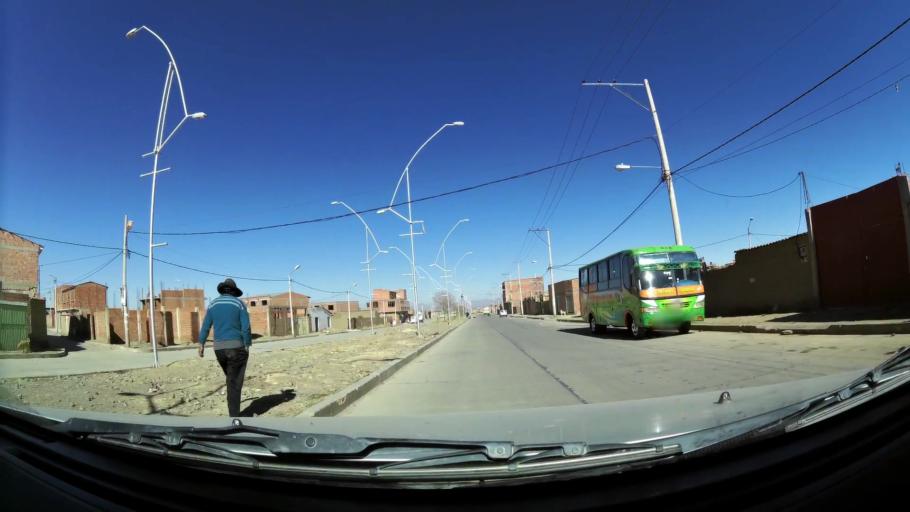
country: BO
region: La Paz
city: La Paz
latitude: -16.5304
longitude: -68.2336
